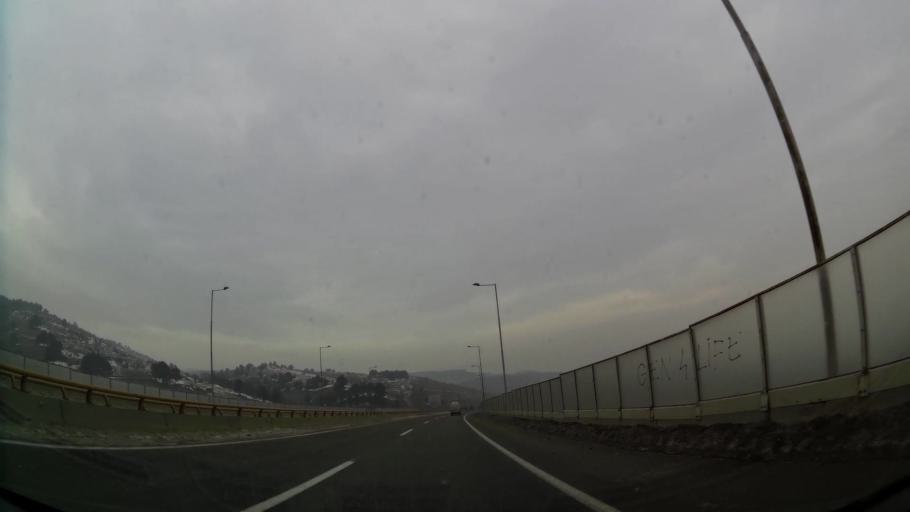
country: MK
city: Kondovo
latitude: 42.0499
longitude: 21.3383
